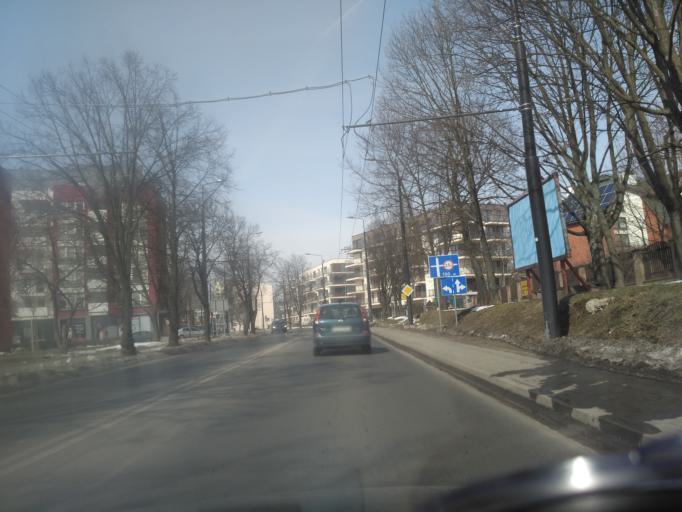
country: PL
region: Lublin Voivodeship
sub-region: Powiat lubelski
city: Lublin
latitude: 51.2570
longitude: 22.5745
